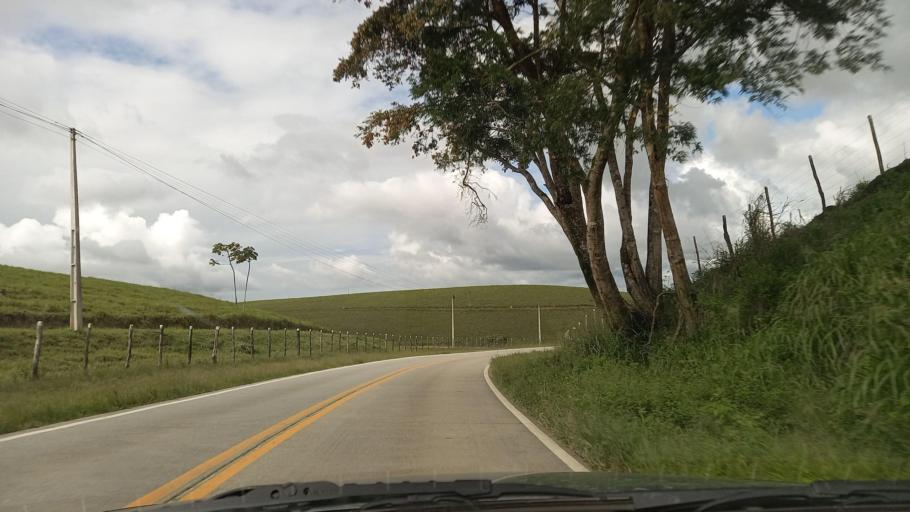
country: BR
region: Pernambuco
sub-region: Quipapa
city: Quipapa
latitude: -8.7749
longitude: -35.9296
